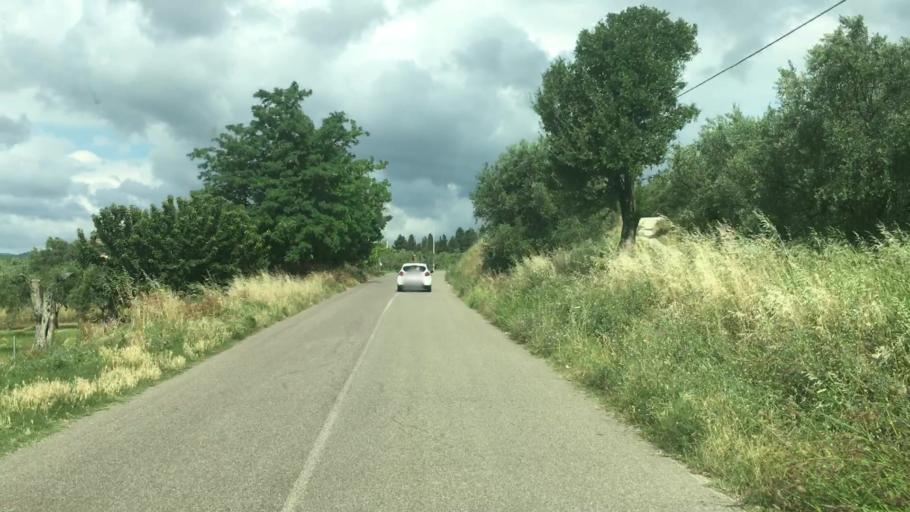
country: IT
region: Basilicate
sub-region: Provincia di Matera
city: San Mauro Forte
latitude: 40.4814
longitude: 16.2605
